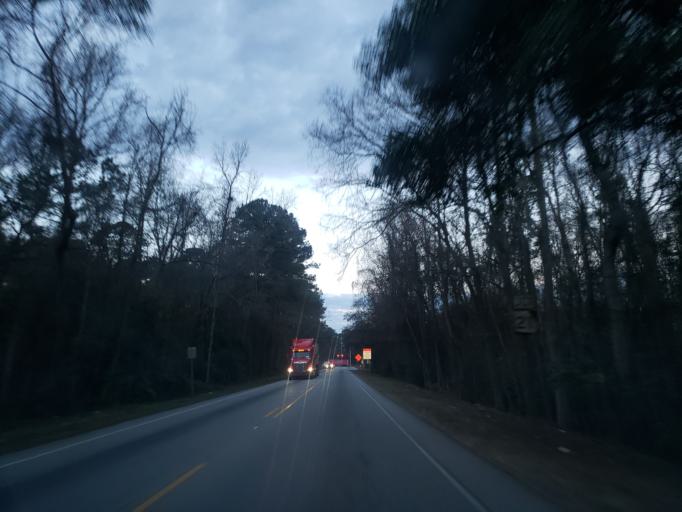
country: US
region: Georgia
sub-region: Chatham County
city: Port Wentworth
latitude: 32.1548
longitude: -81.1777
